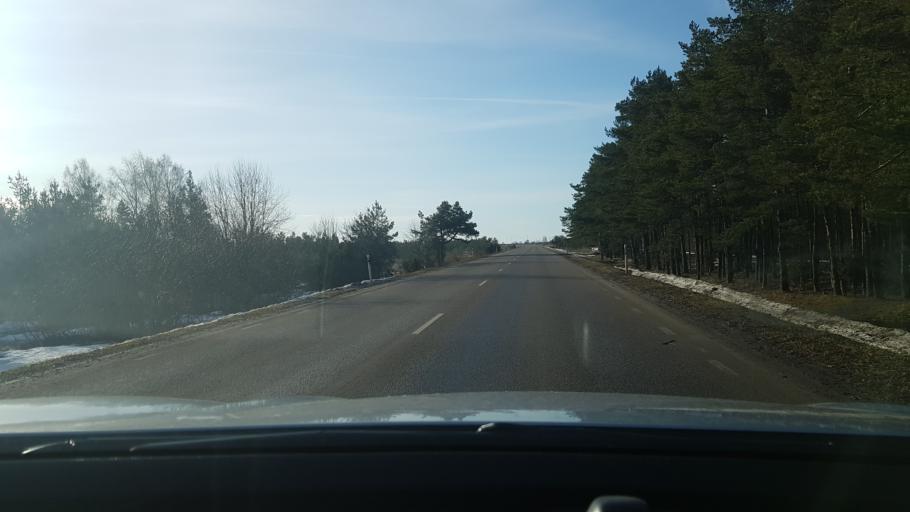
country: EE
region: Saare
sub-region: Kuressaare linn
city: Kuressaare
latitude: 58.2433
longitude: 22.5036
